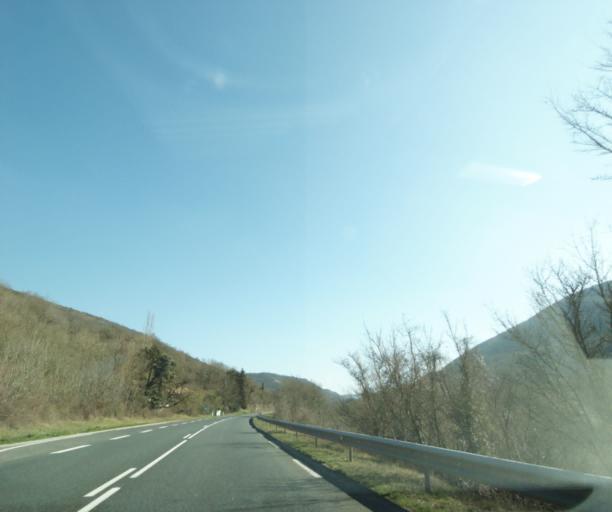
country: FR
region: Midi-Pyrenees
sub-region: Departement de l'Aveyron
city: Saint-Affrique
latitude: 43.9519
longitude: 2.9183
